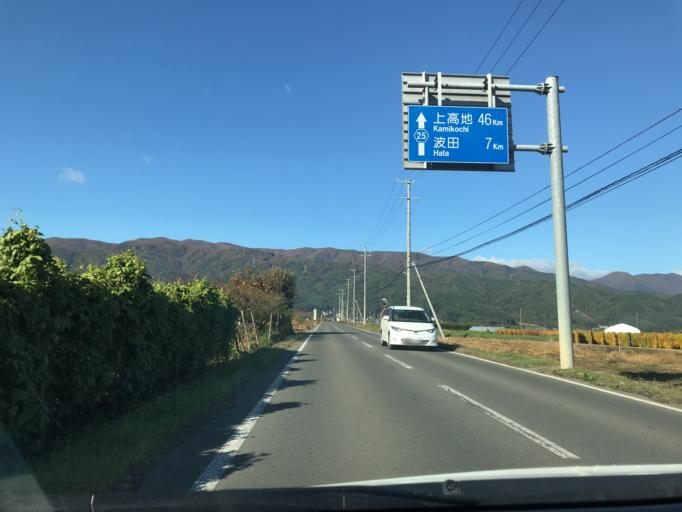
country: JP
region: Nagano
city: Shiojiri
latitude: 36.1580
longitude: 137.8893
